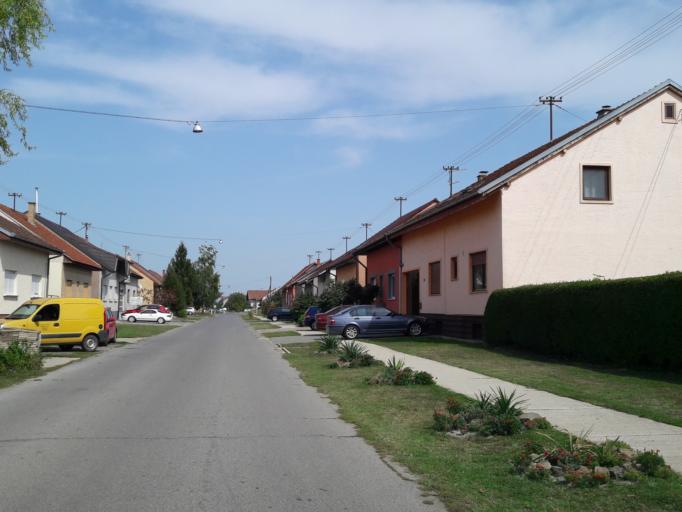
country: HR
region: Osjecko-Baranjska
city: Visnjevac
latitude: 45.5353
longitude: 18.6311
